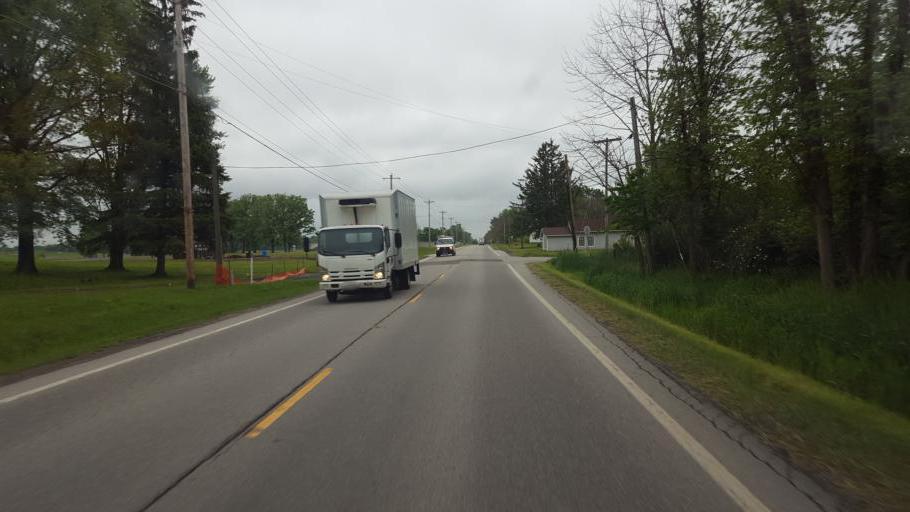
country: US
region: Ohio
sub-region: Wayne County
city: West Salem
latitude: 40.9811
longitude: -82.0970
